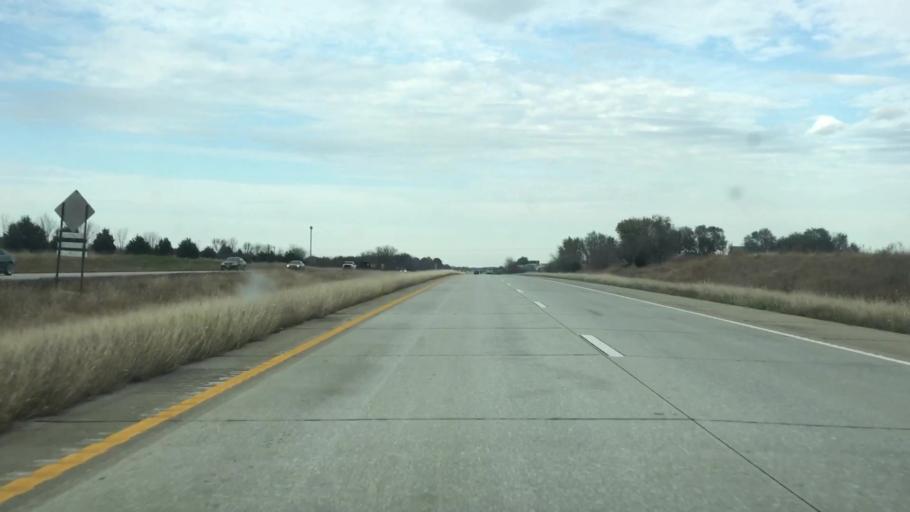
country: US
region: Missouri
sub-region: Henry County
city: Clinton
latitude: 38.2978
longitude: -93.7587
